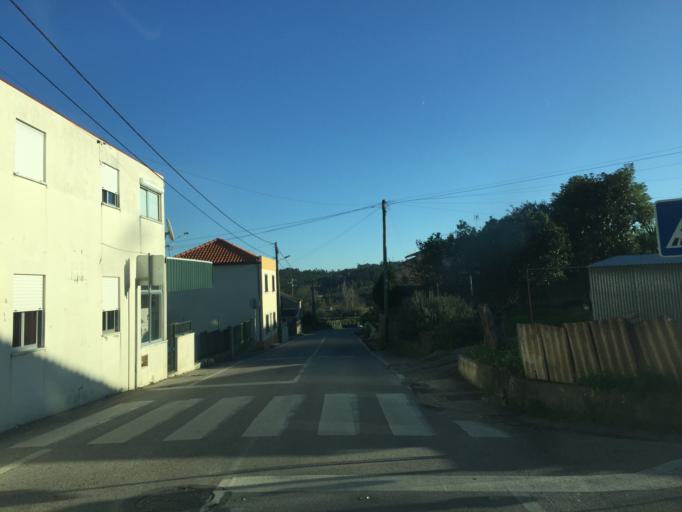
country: PT
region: Coimbra
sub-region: Figueira da Foz
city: Tavarede
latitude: 40.1651
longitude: -8.8189
